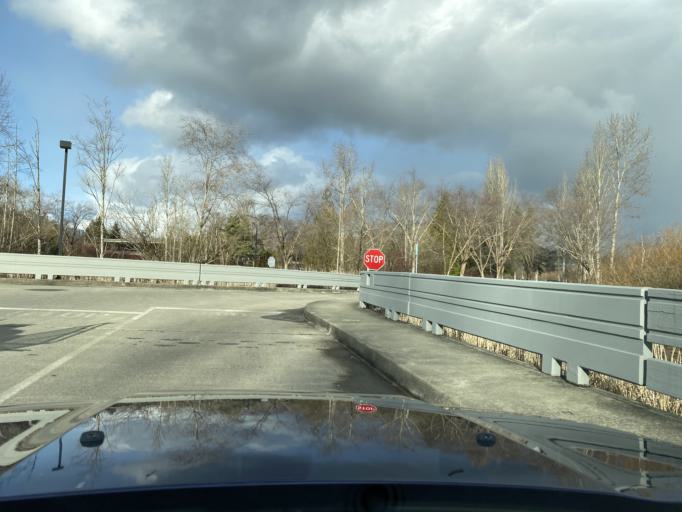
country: US
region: Washington
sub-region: King County
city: Bellevue
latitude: 47.5971
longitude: -122.1896
